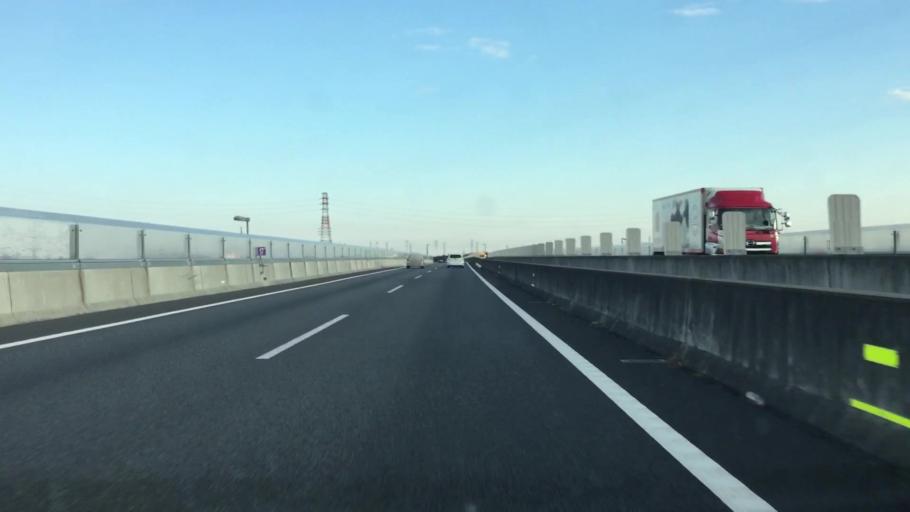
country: JP
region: Gunma
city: Isesaki
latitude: 36.3470
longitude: 139.2465
